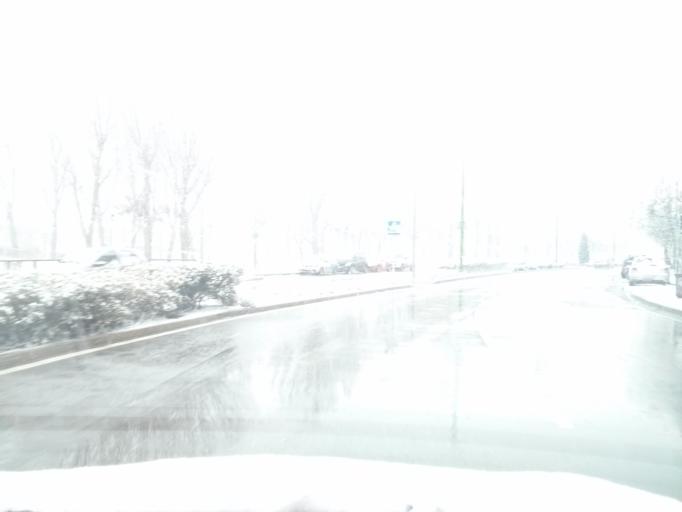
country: ES
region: Castille and Leon
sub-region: Provincia de Burgos
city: Burgos
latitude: 42.3541
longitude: -3.6810
